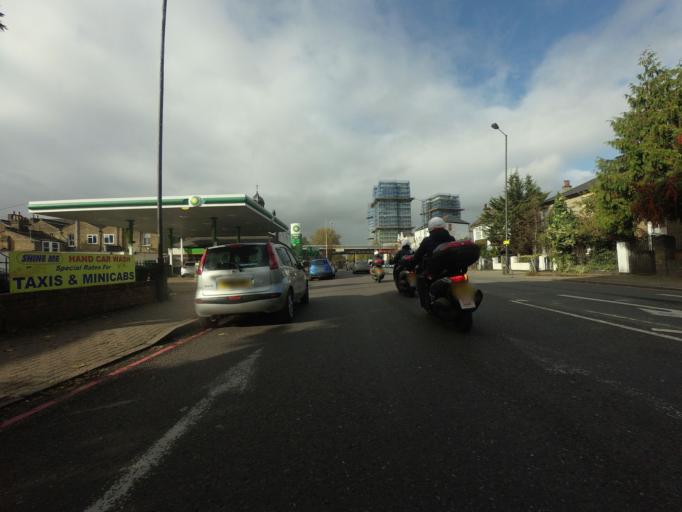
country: GB
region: England
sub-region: Greater London
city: Camberwell
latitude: 51.4781
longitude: -0.0529
